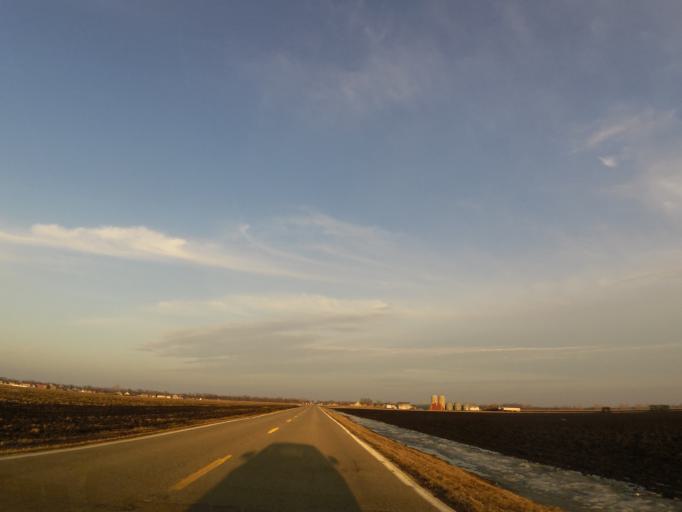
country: US
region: North Dakota
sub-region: Grand Forks County
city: Grand Forks
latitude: 47.8603
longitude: -97.0385
